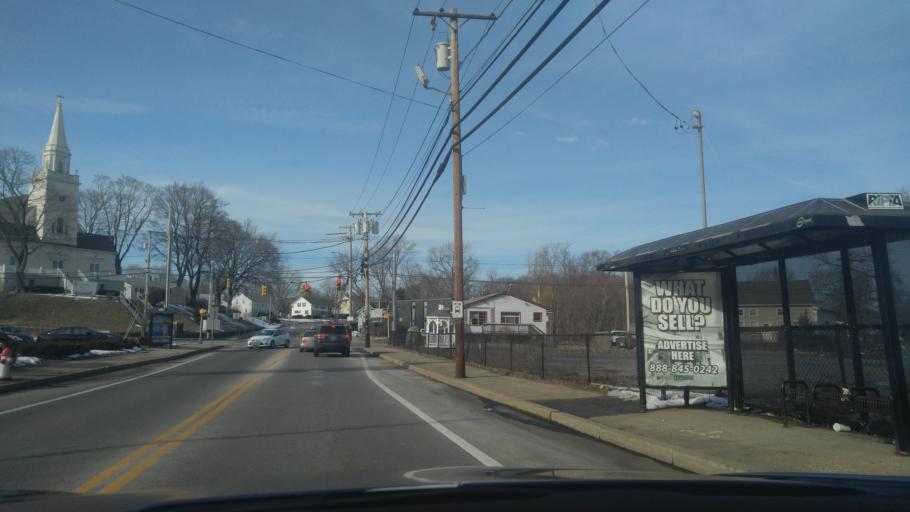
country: US
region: Rhode Island
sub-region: Kent County
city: West Warwick
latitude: 41.7238
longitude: -71.4913
